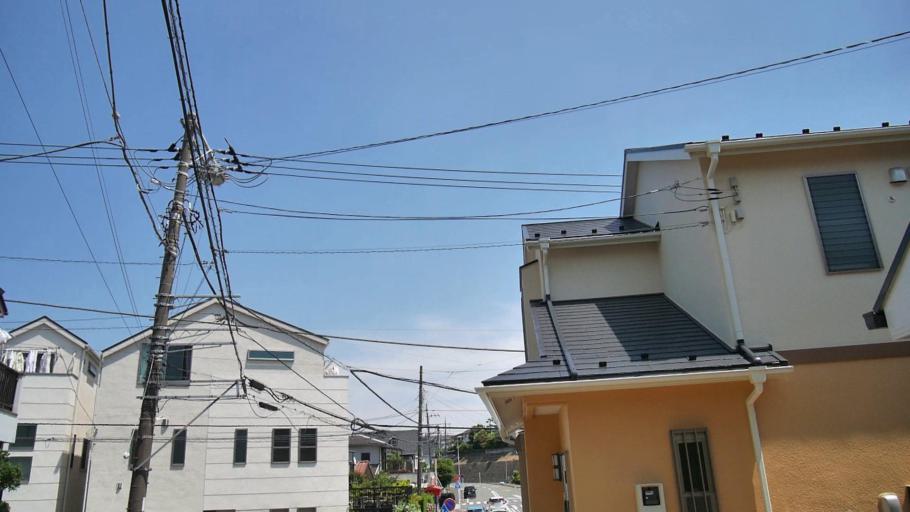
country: JP
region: Kanagawa
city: Fujisawa
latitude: 35.3974
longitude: 139.5174
